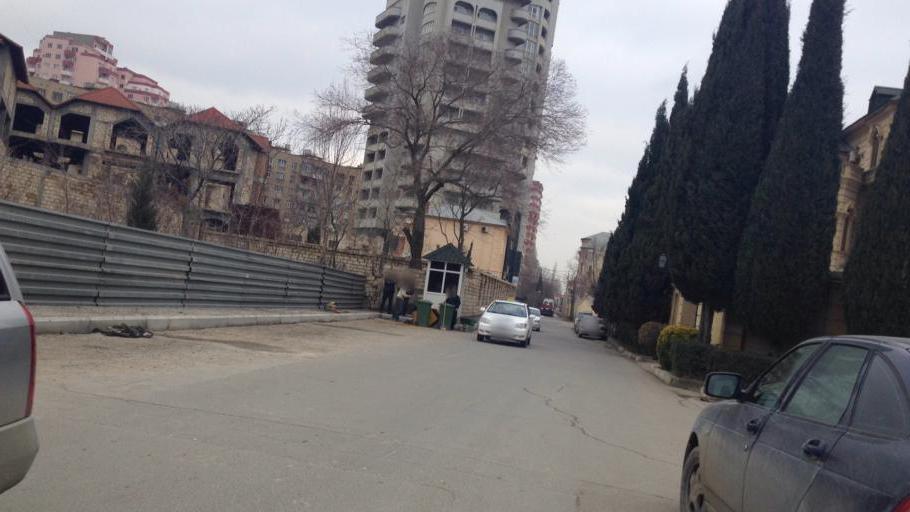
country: AZ
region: Baki
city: Bilajari
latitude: 40.3940
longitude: 49.8207
